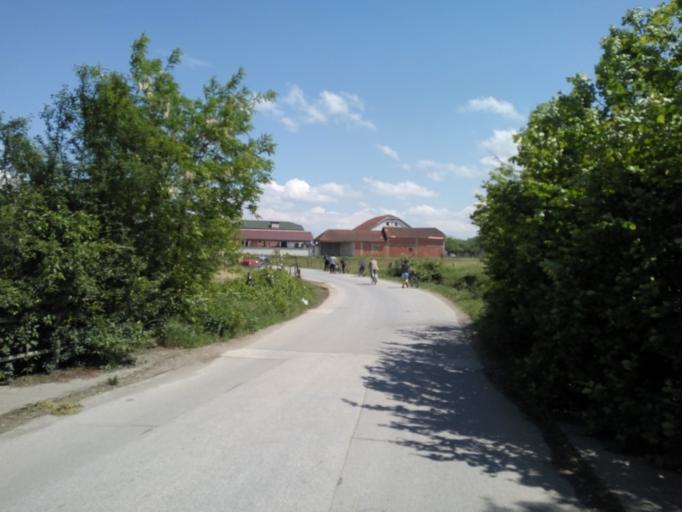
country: XK
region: Gjakova
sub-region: Komuna e Gjakoves
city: Gjakove
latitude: 42.3626
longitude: 20.4302
